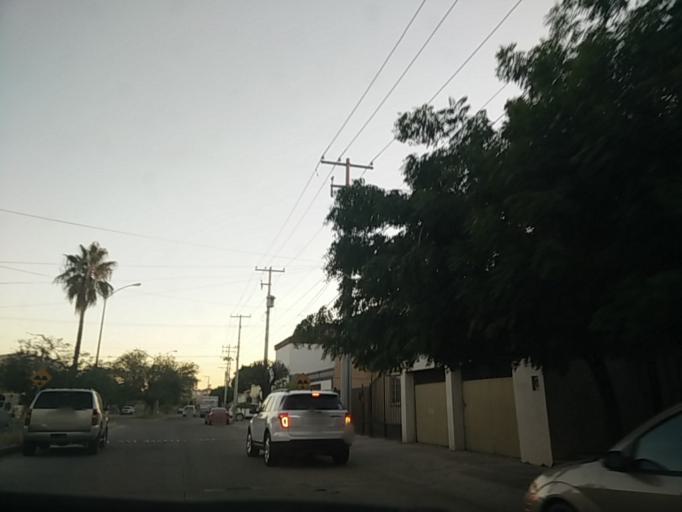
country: MX
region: Sonora
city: Hermosillo
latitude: 29.0784
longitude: -110.9942
